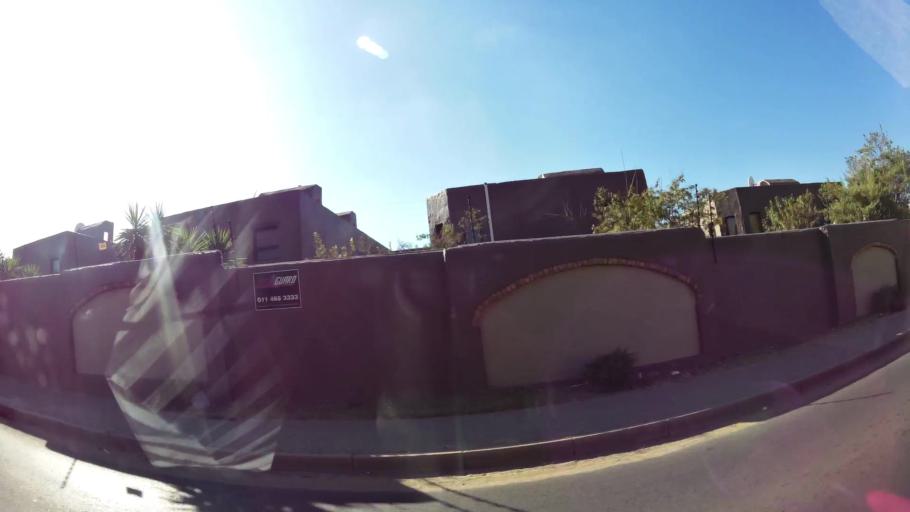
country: ZA
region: Gauteng
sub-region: West Rand District Municipality
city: Muldersdriseloop
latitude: -26.0495
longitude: 27.9600
